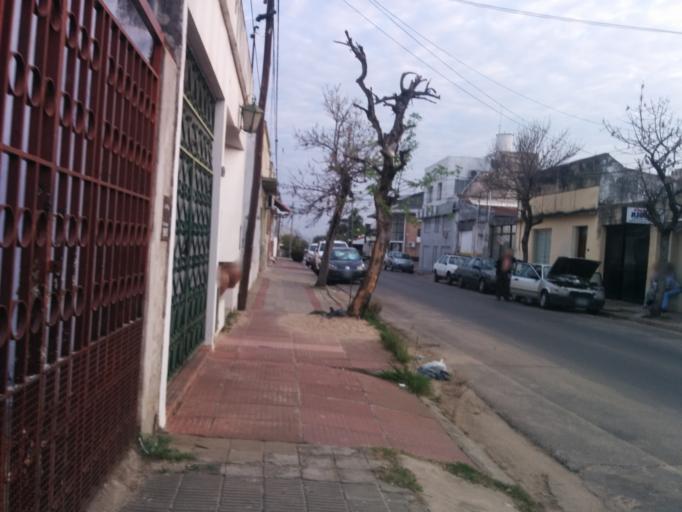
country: AR
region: Entre Rios
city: Concordia
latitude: -31.3904
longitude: -58.0205
